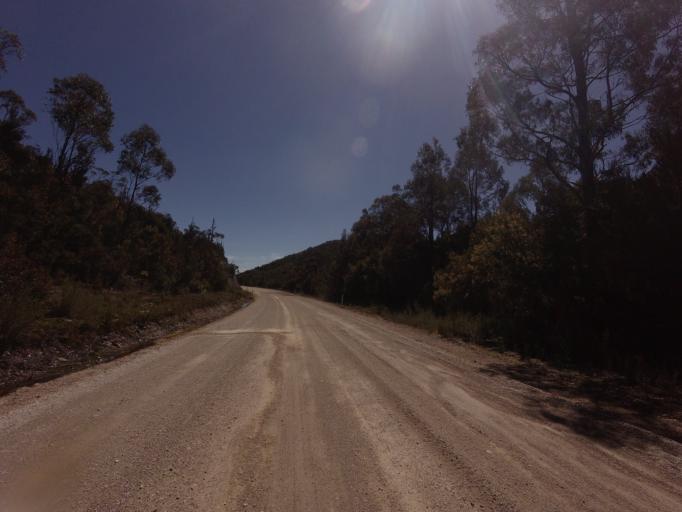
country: AU
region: Tasmania
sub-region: Huon Valley
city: Geeveston
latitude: -42.8212
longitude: 146.3900
